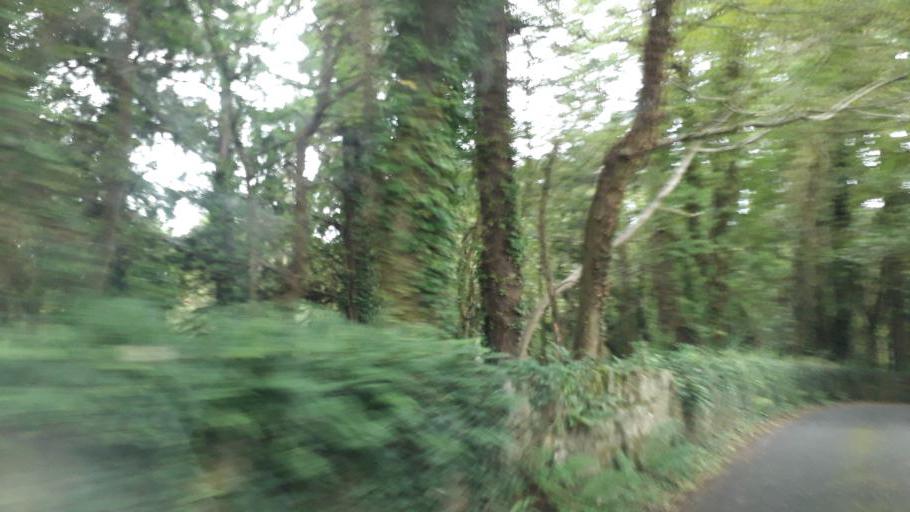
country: IE
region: Leinster
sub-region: Wicklow
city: Enniskerry
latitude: 53.1722
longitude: -6.1972
